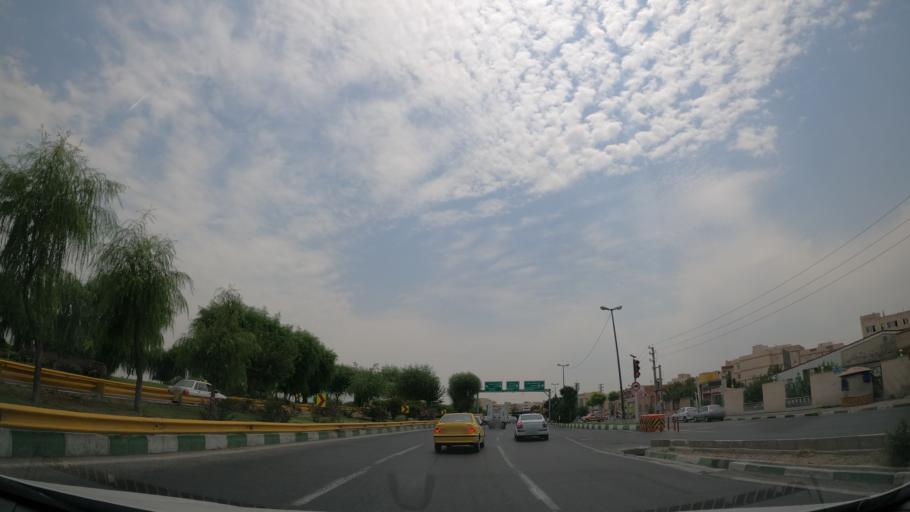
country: IR
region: Tehran
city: Tehran
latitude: 35.6795
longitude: 51.3371
